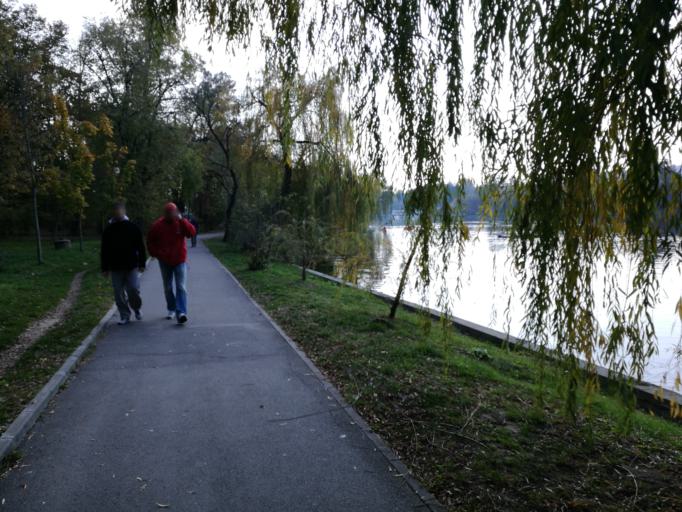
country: RO
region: Bucuresti
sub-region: Municipiul Bucuresti
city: Bucuresti
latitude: 44.4786
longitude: 26.0786
